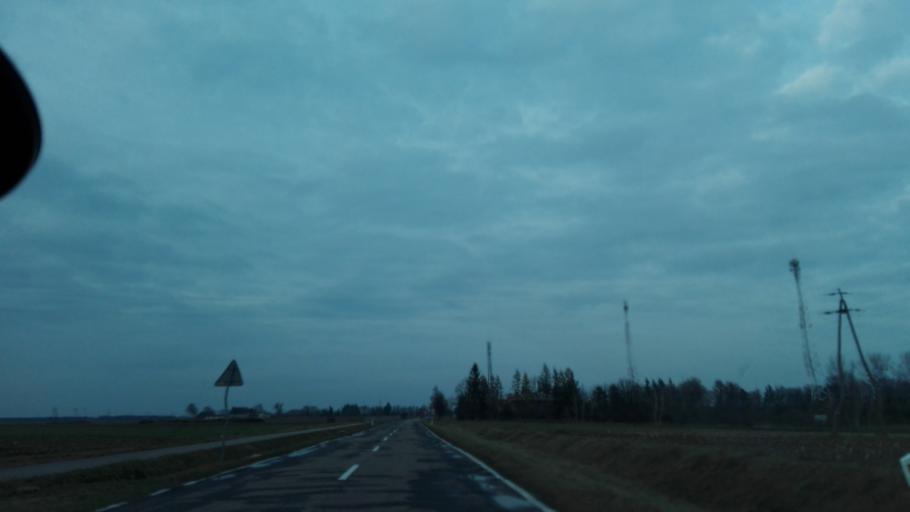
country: PL
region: Lublin Voivodeship
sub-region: Powiat bialski
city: Slawatycze
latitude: 51.6804
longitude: 23.5070
